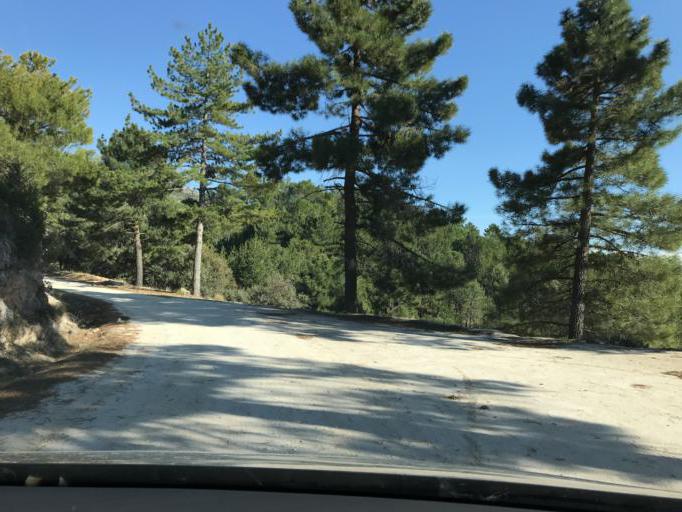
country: ES
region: Andalusia
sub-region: Provincia de Granada
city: Beas de Granada
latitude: 37.2520
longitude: -3.4657
